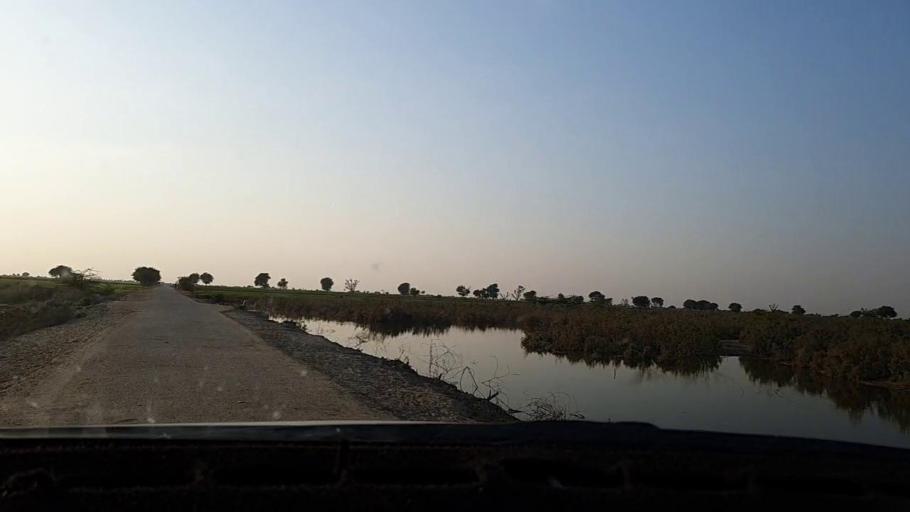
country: PK
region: Sindh
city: Tando Mittha Khan
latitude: 25.8679
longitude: 69.2647
